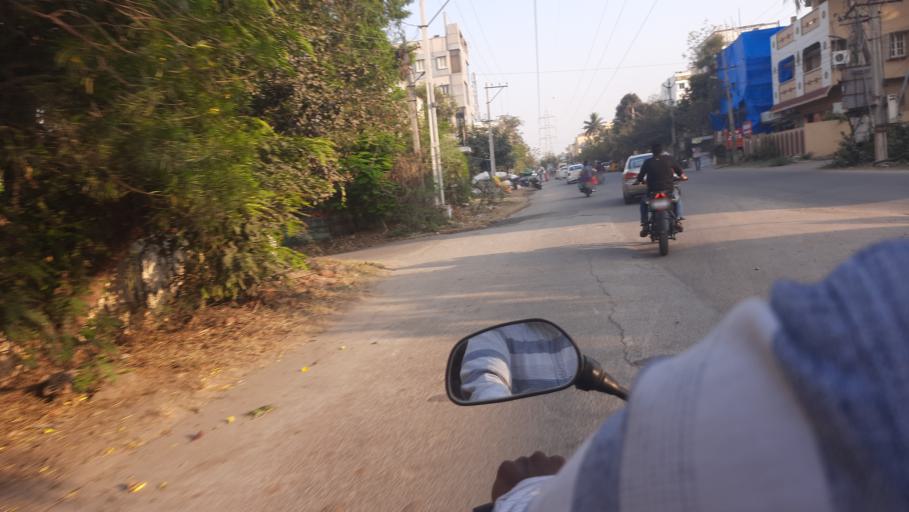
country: IN
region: Telangana
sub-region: Rangareddi
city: Secunderabad
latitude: 17.4950
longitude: 78.5449
